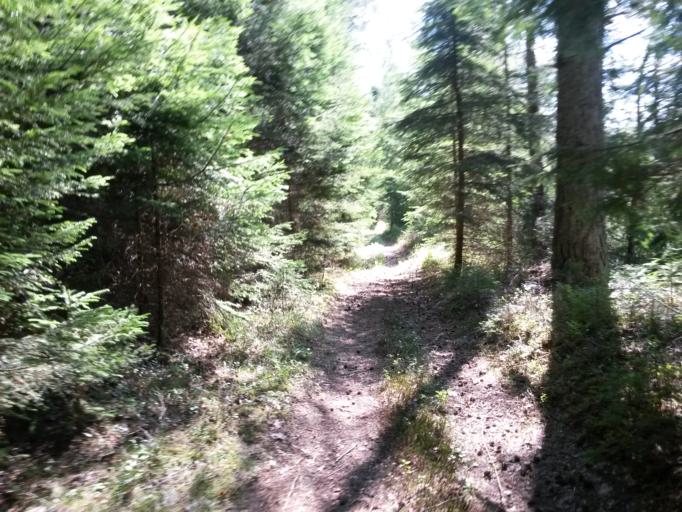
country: SE
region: Vaestra Goetaland
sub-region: Vargarda Kommun
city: Jonstorp
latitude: 57.9663
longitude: 12.6845
